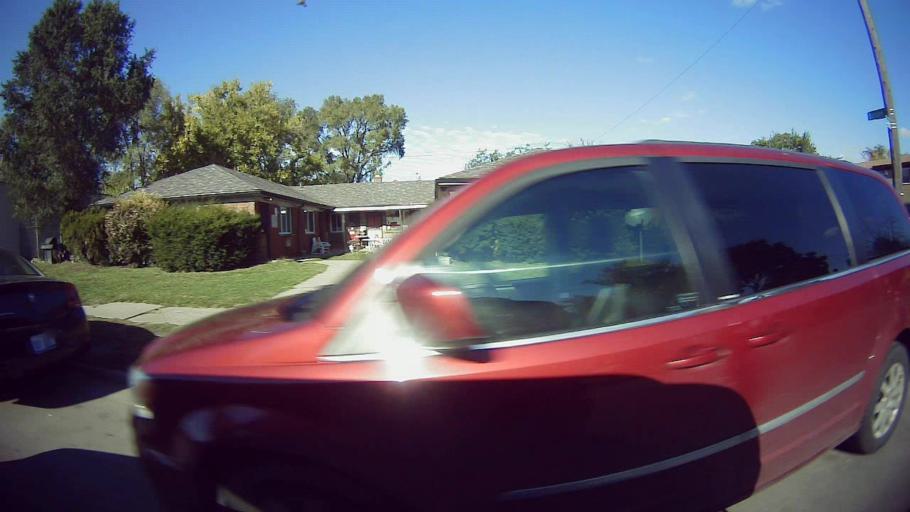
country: US
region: Michigan
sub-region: Wayne County
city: Dearborn
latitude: 42.3511
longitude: -83.1948
